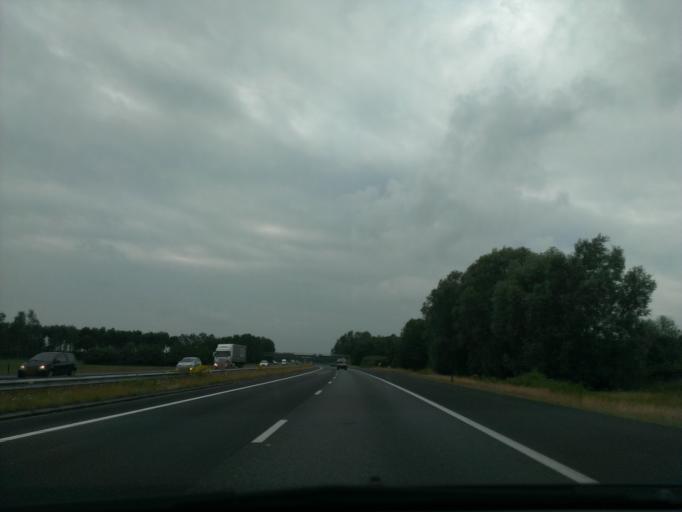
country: NL
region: Drenthe
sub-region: Gemeente Meppel
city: Meppel
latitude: 52.6860
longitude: 6.2415
